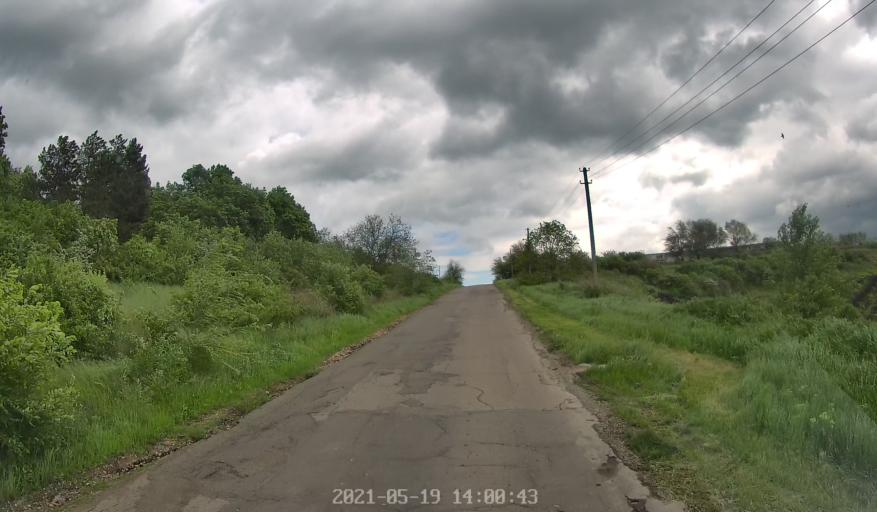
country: MD
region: Chisinau
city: Chisinau
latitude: 47.0340
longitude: 28.9333
